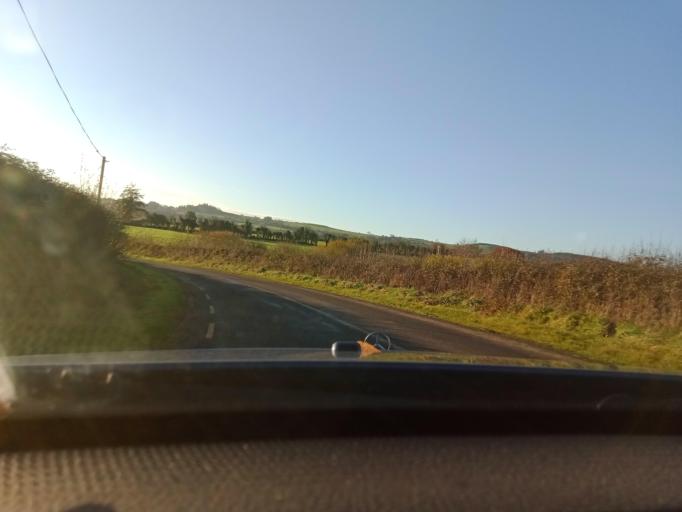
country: IE
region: Leinster
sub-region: Kilkenny
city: Callan
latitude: 52.4792
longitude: -7.3914
